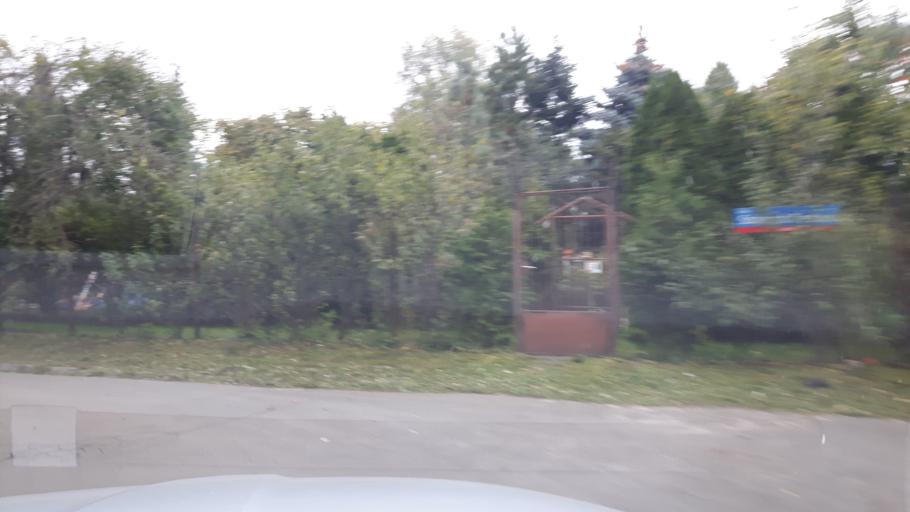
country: PL
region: Masovian Voivodeship
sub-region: Warszawa
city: Praga Poludnie
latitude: 52.2503
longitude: 21.0993
